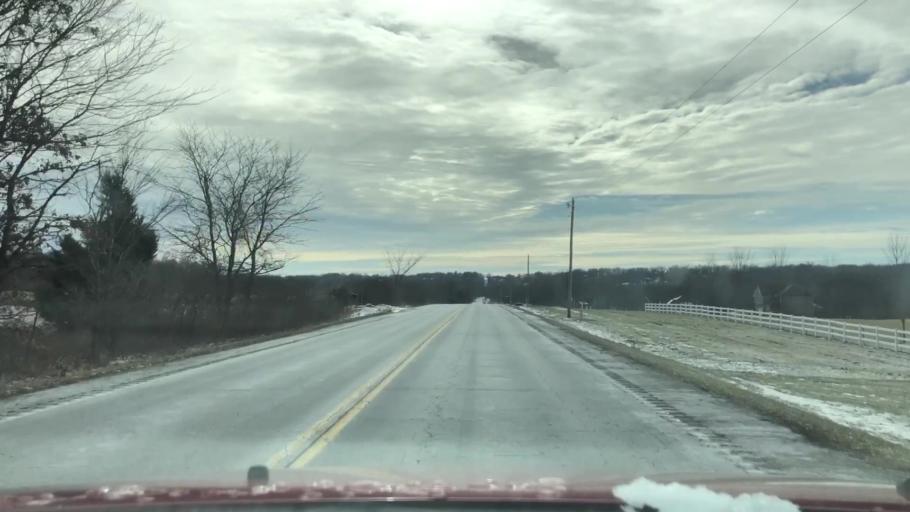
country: US
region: Missouri
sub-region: Jackson County
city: Lone Jack
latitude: 38.9086
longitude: -94.1335
